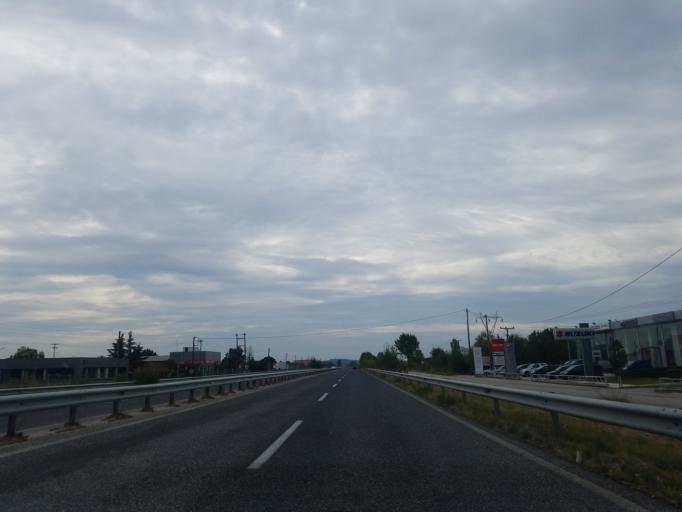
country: GR
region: Thessaly
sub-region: Trikala
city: Vasiliki
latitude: 39.6091
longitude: 21.7226
